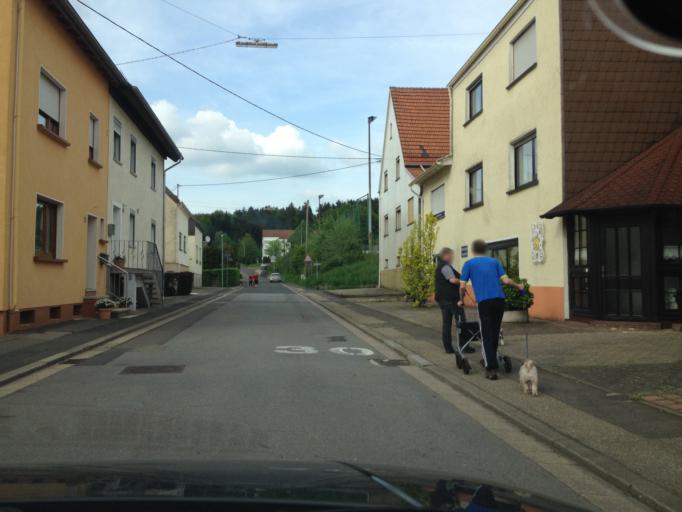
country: DE
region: Saarland
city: Mainzweiler
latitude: 49.3920
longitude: 7.1168
